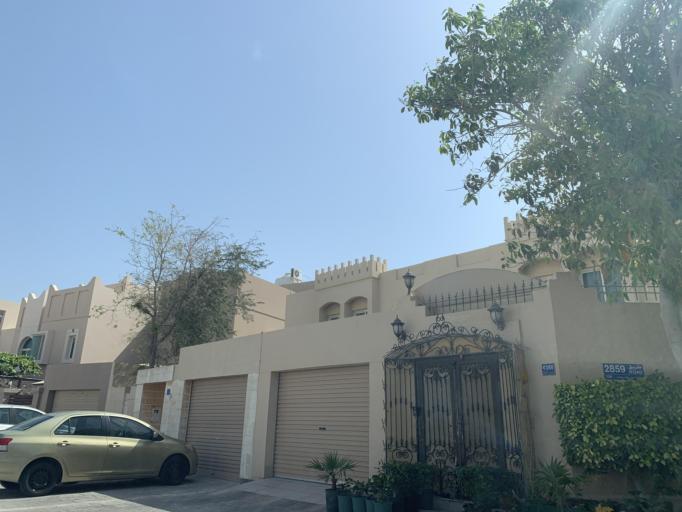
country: BH
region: Muharraq
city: Al Muharraq
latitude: 26.2723
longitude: 50.5973
